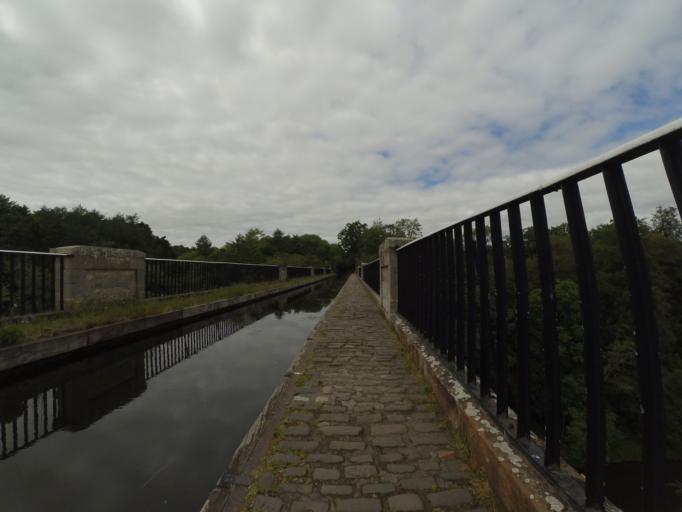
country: GB
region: Scotland
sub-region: West Lothian
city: Linlithgow
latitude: 55.9644
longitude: -3.6564
